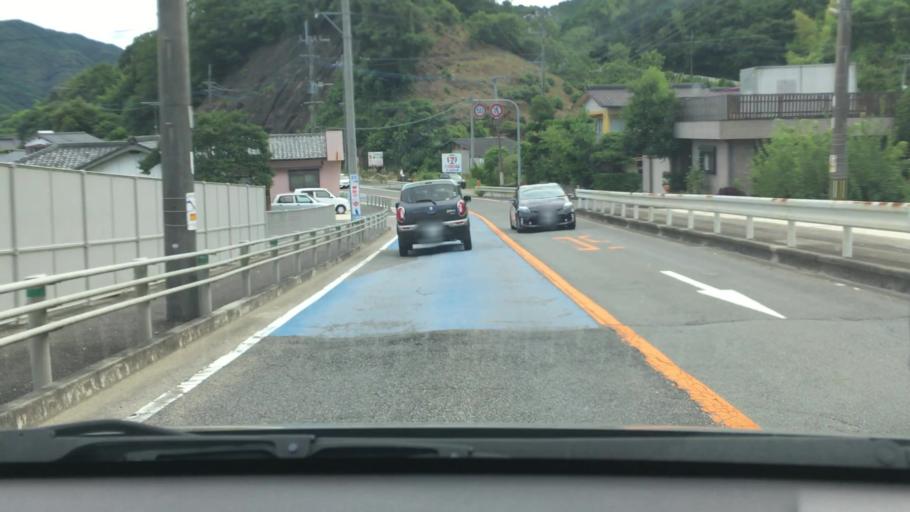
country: JP
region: Nagasaki
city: Sasebo
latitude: 32.9905
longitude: 129.7379
